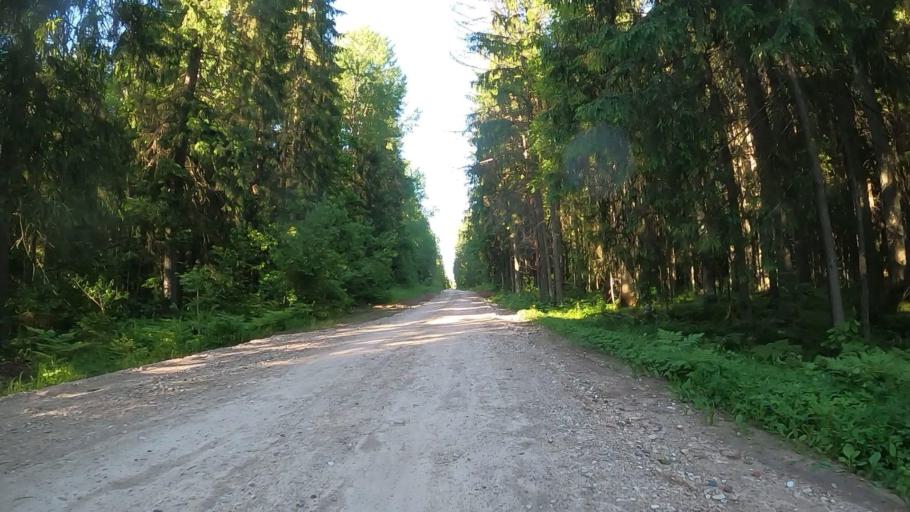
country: LV
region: Ogre
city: Ogre
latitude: 56.8298
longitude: 24.5950
